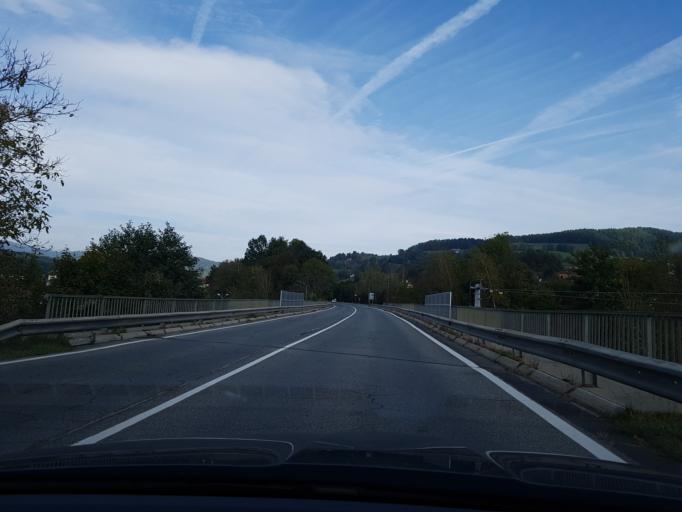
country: AT
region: Carinthia
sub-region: Politischer Bezirk Feldkirchen
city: Feldkirchen in Karnten
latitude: 46.7208
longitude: 14.1053
